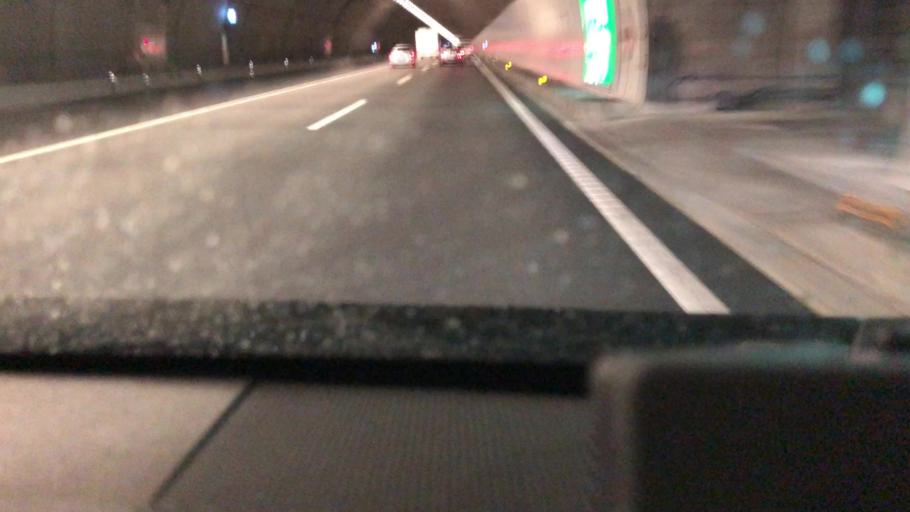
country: JP
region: Shizuoka
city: Fujinomiya
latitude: 35.1620
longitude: 138.5665
